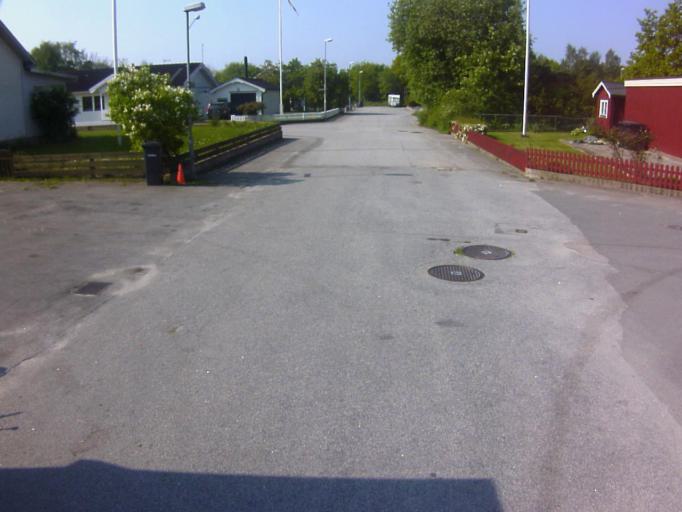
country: SE
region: Blekinge
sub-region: Solvesborgs Kommun
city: Soelvesborg
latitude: 56.0071
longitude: 14.7304
